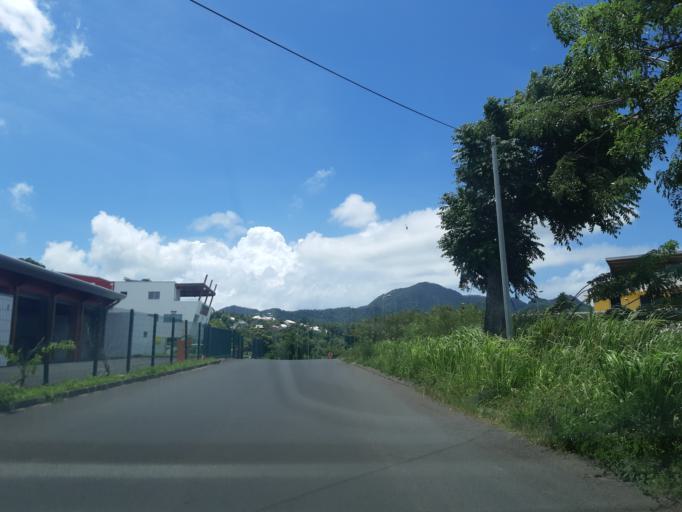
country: GP
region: Guadeloupe
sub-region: Guadeloupe
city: Basse-Terre
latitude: 16.0081
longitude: -61.7160
